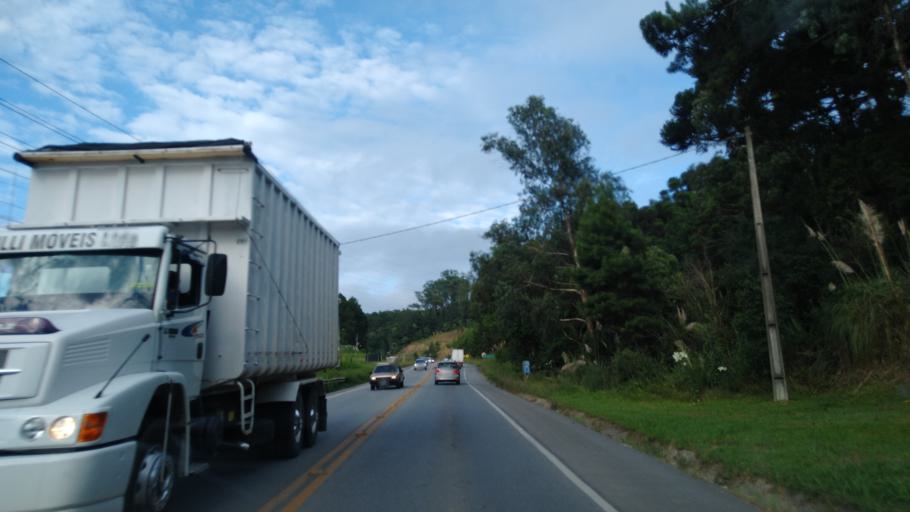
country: BR
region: Santa Catarina
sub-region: Sao Bento Do Sul
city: Sao Bento do Sul
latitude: -26.2284
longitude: -49.4216
